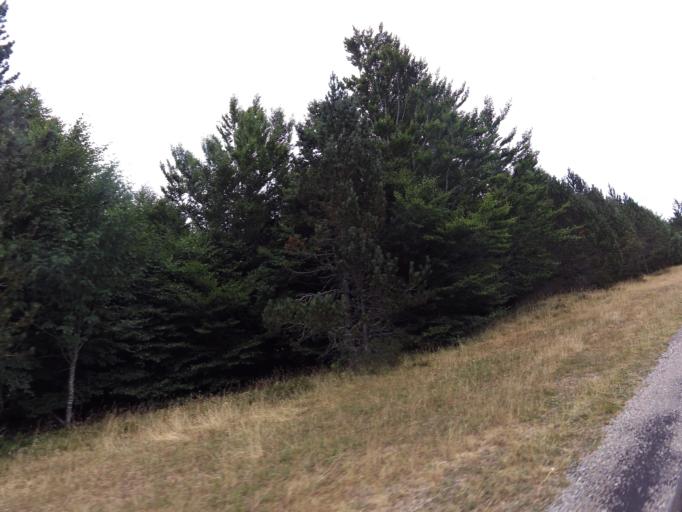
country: FR
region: Languedoc-Roussillon
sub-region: Departement du Gard
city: Valleraugue
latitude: 44.0765
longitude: 3.5799
